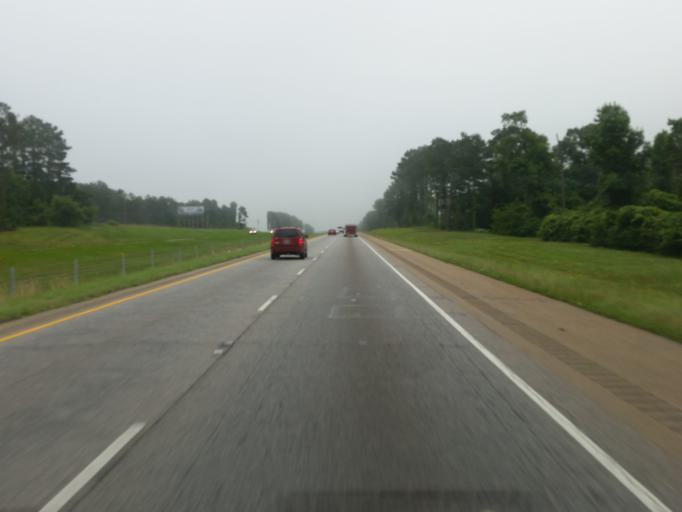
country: US
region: Louisiana
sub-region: Webster Parish
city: Minden
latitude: 32.5866
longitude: -93.2776
